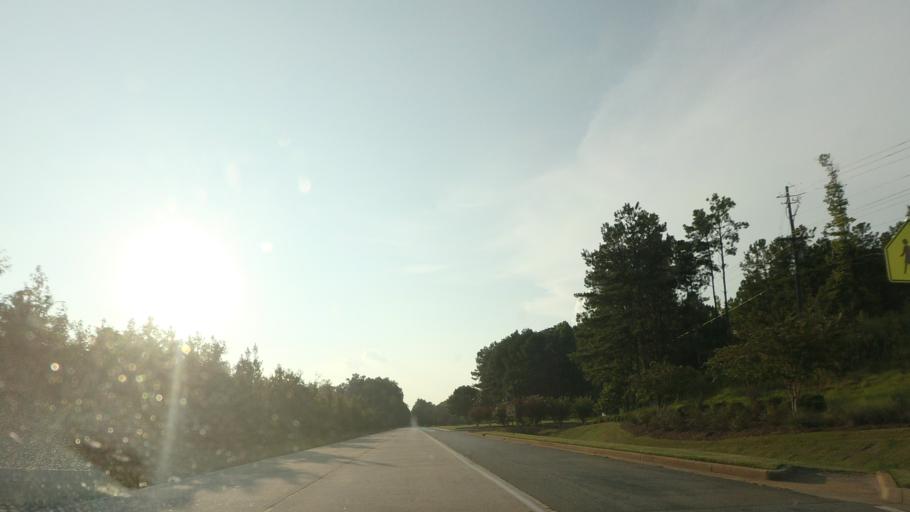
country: US
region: Georgia
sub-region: Bibb County
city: Macon
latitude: 32.9356
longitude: -83.7265
